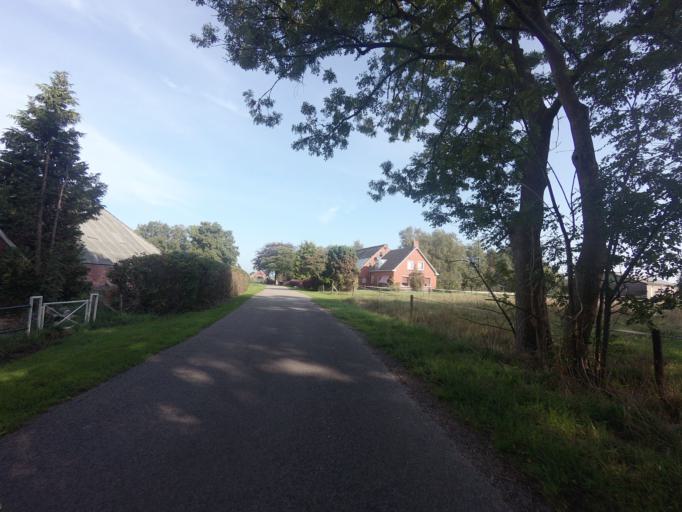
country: NL
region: Groningen
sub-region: Gemeente Leek
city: Leek
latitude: 53.1570
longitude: 6.4333
